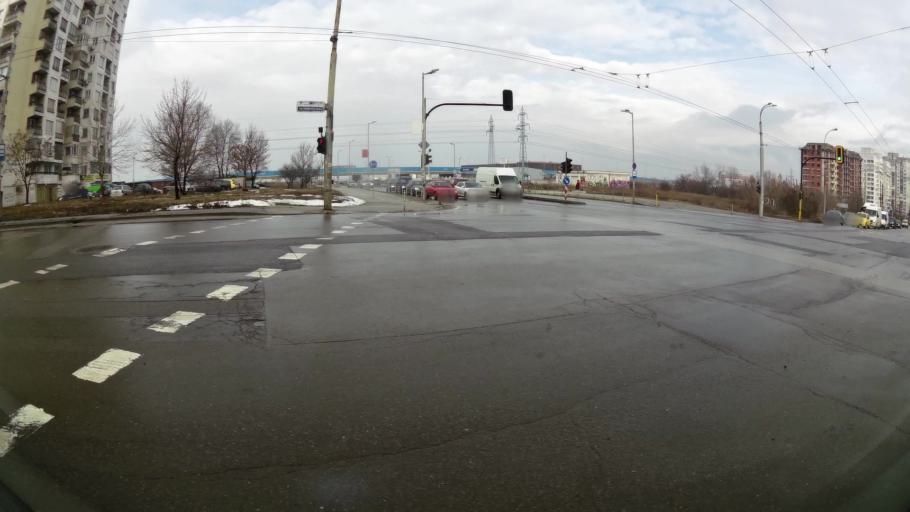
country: BG
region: Sofiya
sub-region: Obshtina Bozhurishte
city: Bozhurishte
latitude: 42.7250
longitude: 23.2440
